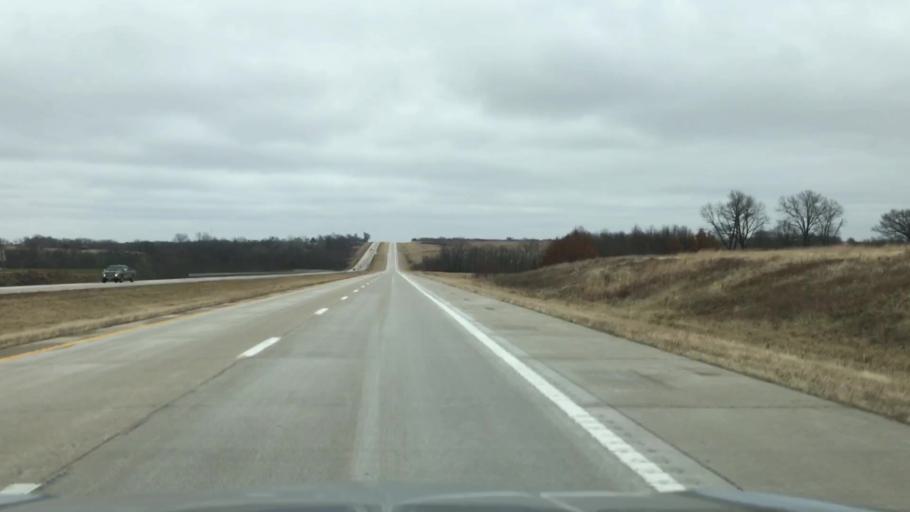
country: US
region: Missouri
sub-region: Livingston County
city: Chillicothe
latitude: 39.7376
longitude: -93.7064
